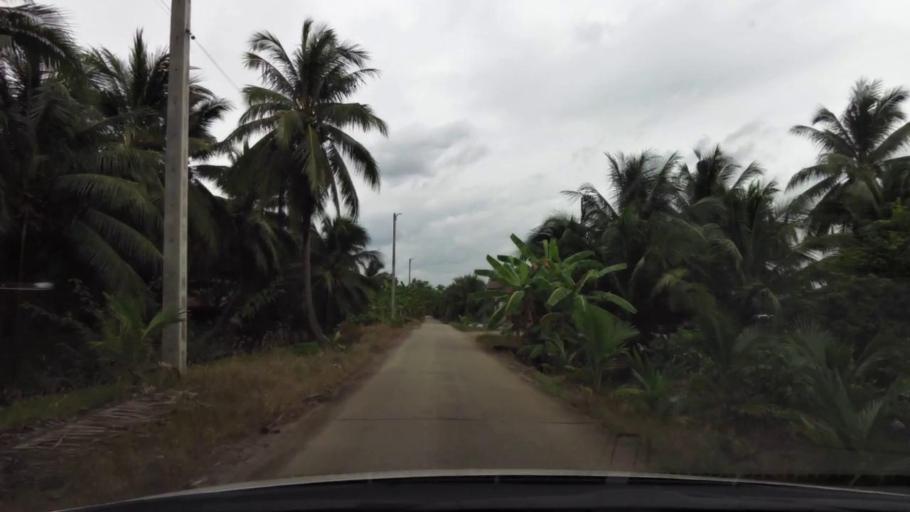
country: TH
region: Ratchaburi
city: Damnoen Saduak
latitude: 13.5561
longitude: 100.0074
